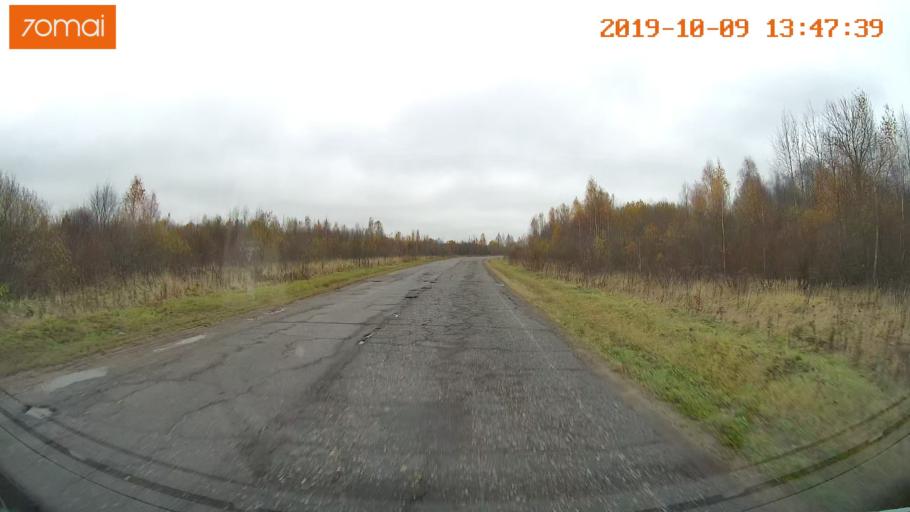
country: RU
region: Kostroma
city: Buy
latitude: 58.3941
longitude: 41.2255
